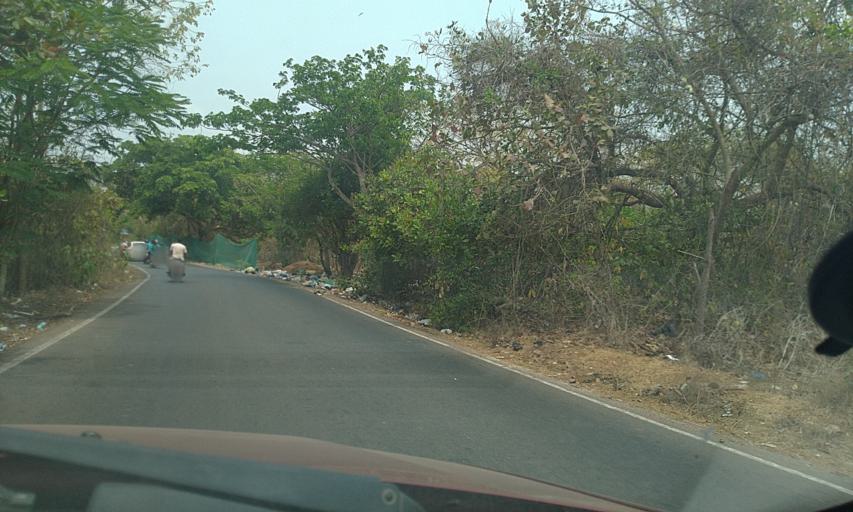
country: IN
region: Goa
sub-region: North Goa
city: Mapuca
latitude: 15.6115
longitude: 73.7955
